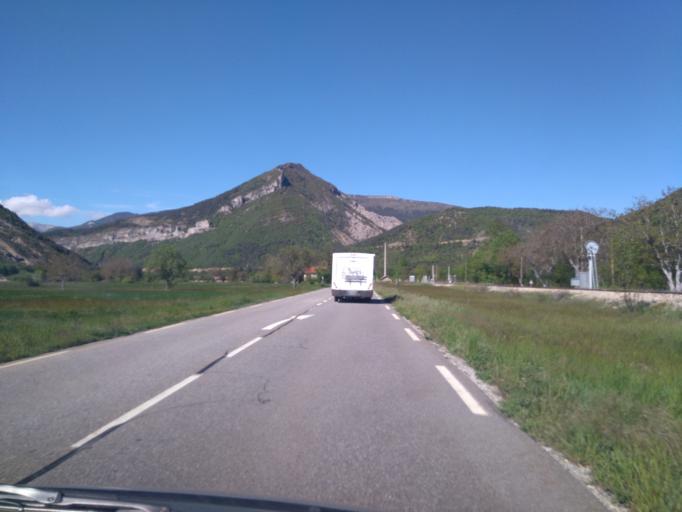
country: FR
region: Provence-Alpes-Cote d'Azur
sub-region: Departement des Hautes-Alpes
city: Veynes
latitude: 44.5328
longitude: 5.7727
